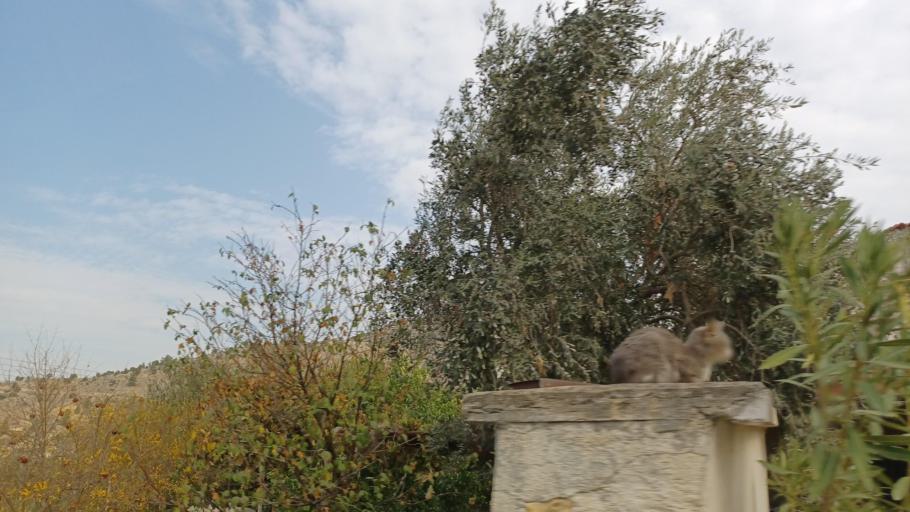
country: CY
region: Lefkosia
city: Klirou
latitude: 35.0438
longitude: 33.1245
